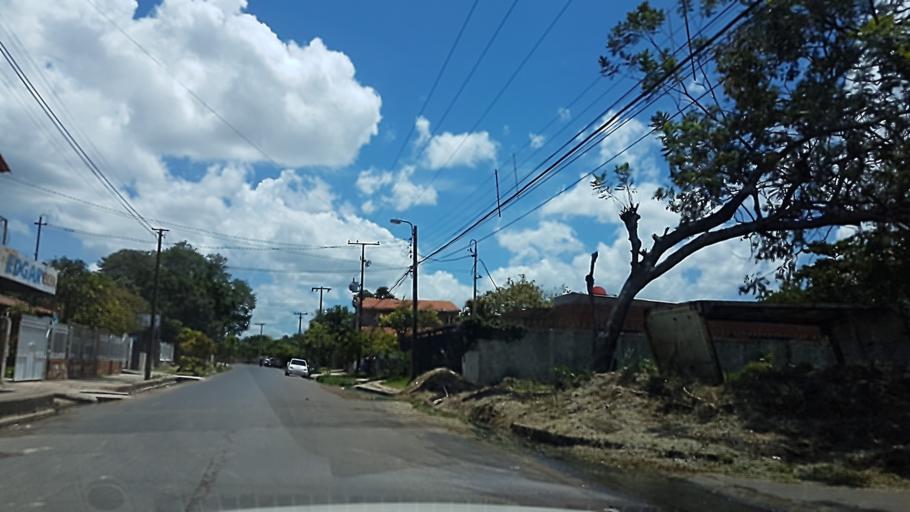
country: PY
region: Central
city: Colonia Mariano Roque Alonso
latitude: -25.2219
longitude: -57.5251
